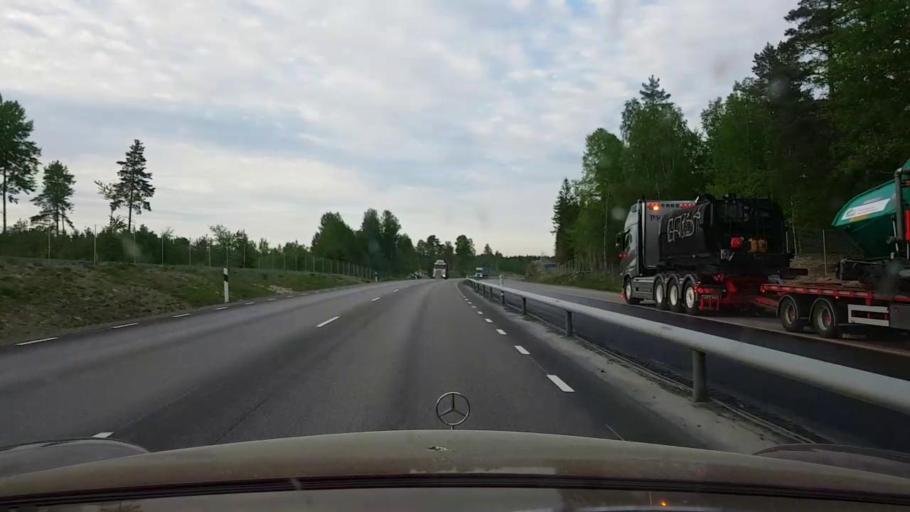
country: SE
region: OErebro
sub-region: Askersunds Kommun
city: Askersund
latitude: 58.9176
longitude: 14.9803
